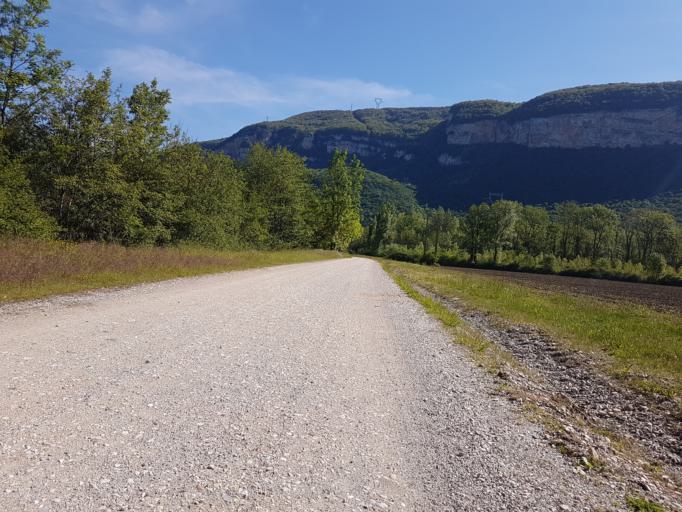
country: FR
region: Rhone-Alpes
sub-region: Departement de l'Ain
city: Villebois
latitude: 45.8220
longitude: 5.4353
